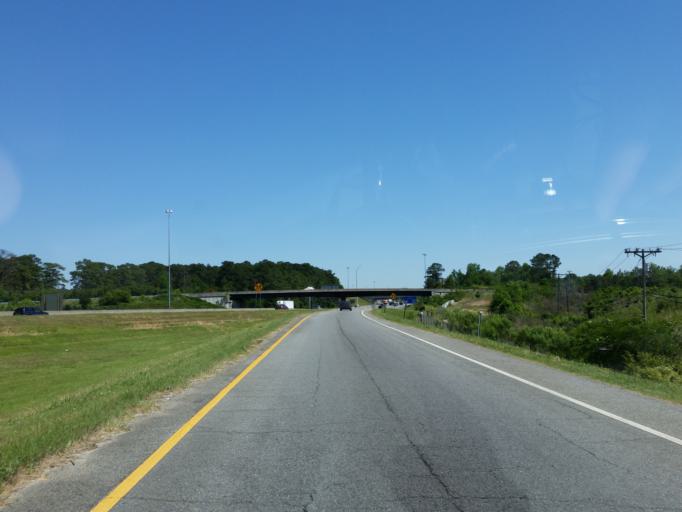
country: US
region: Georgia
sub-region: Tift County
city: Tifton
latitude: 31.4483
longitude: -83.5317
